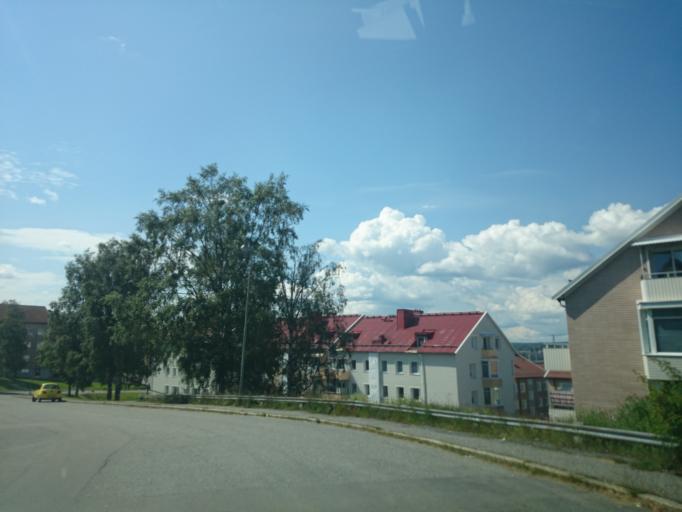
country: SE
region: Vaesternorrland
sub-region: Haernoesands Kommun
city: Haernoesand
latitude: 62.6383
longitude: 17.9515
